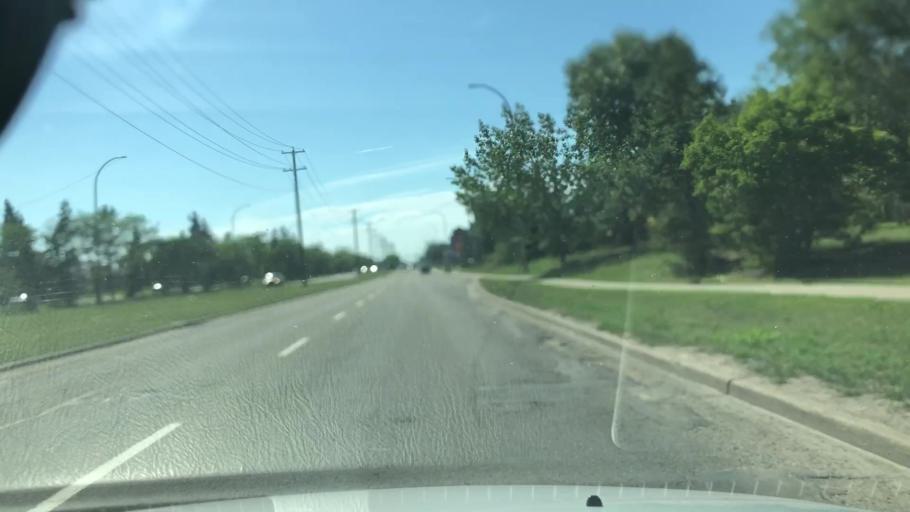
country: CA
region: Alberta
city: Edmonton
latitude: 53.5996
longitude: -113.5289
